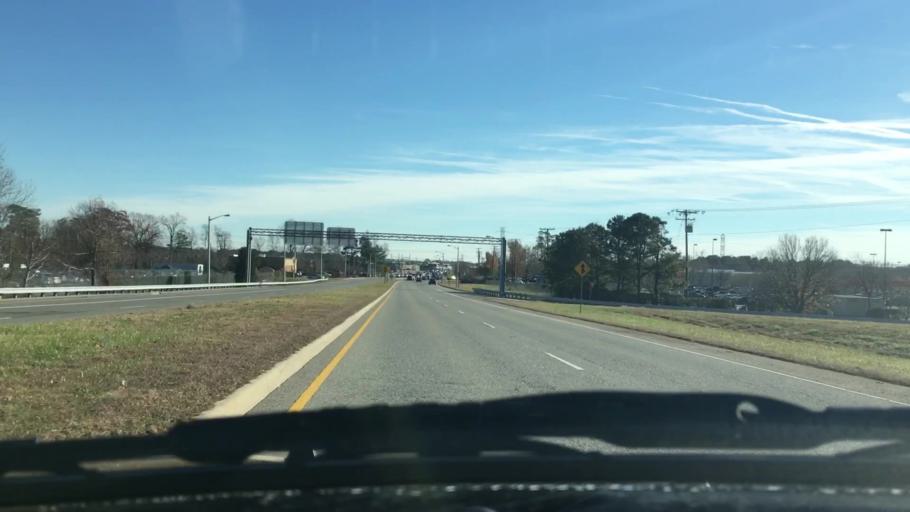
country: US
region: Virginia
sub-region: City of Portsmouth
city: Portsmouth Heights
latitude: 36.8845
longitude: -76.4276
